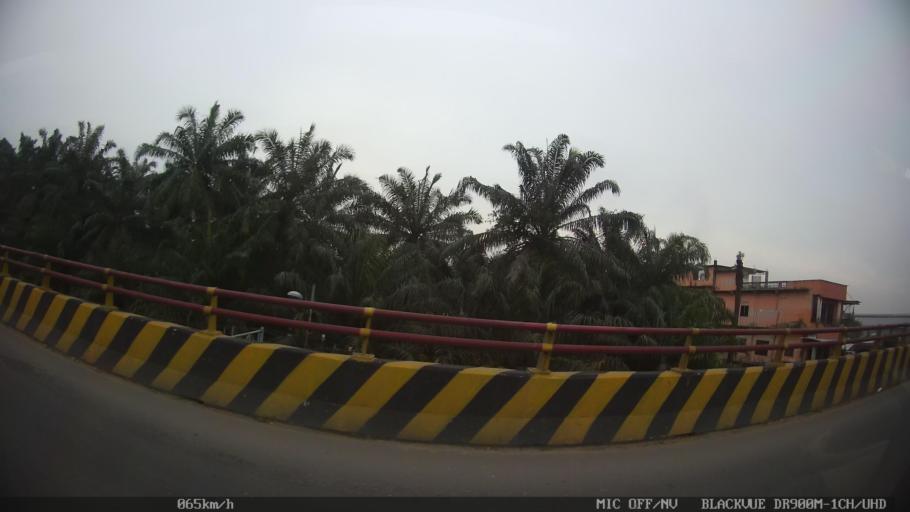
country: ID
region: North Sumatra
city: Deli Tua
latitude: 3.5371
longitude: 98.7153
